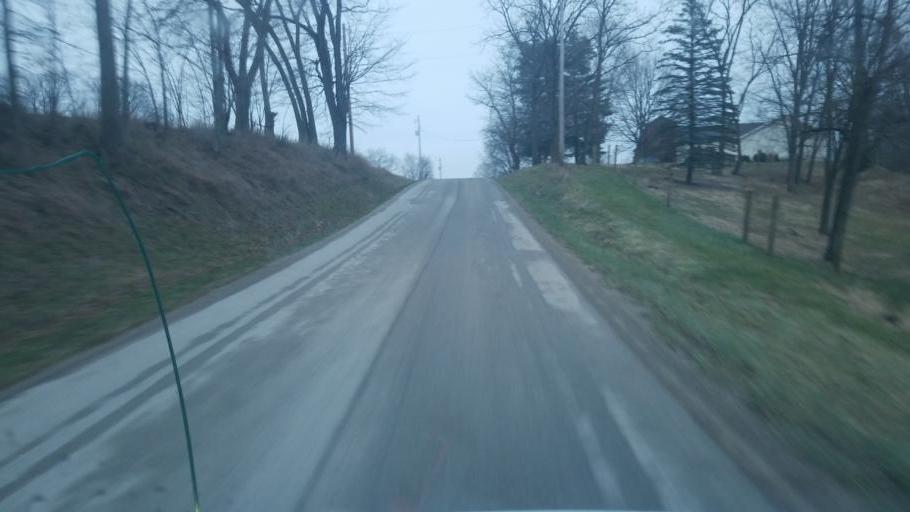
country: US
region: Ohio
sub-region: Seneca County
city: Tiffin
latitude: 40.9915
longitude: -83.1678
